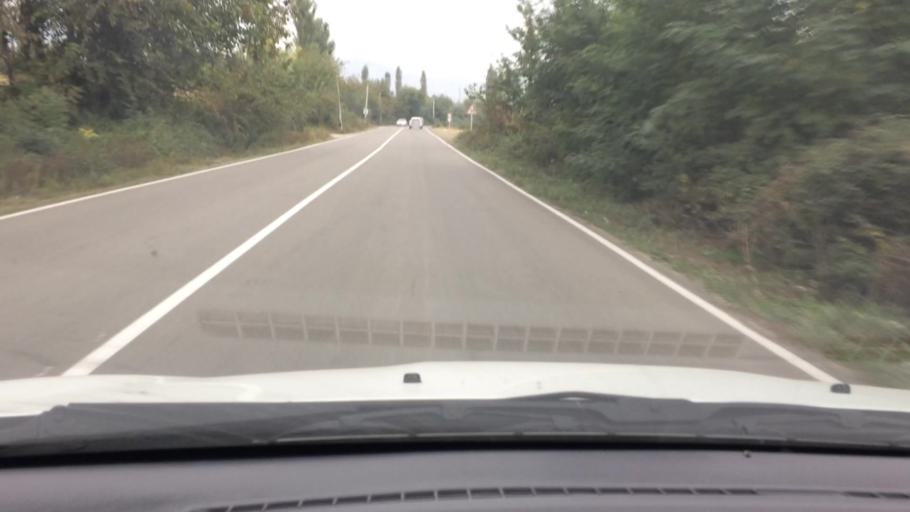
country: AM
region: Tavush
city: Bagratashen
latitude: 41.2619
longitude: 44.7956
